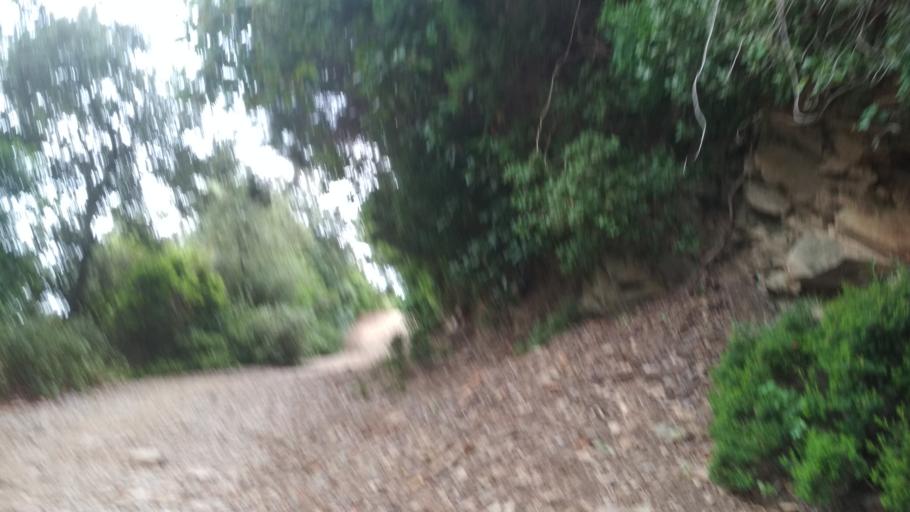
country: ES
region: Catalonia
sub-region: Provincia de Barcelona
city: Horta-Guinardo
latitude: 41.4424
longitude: 2.1373
